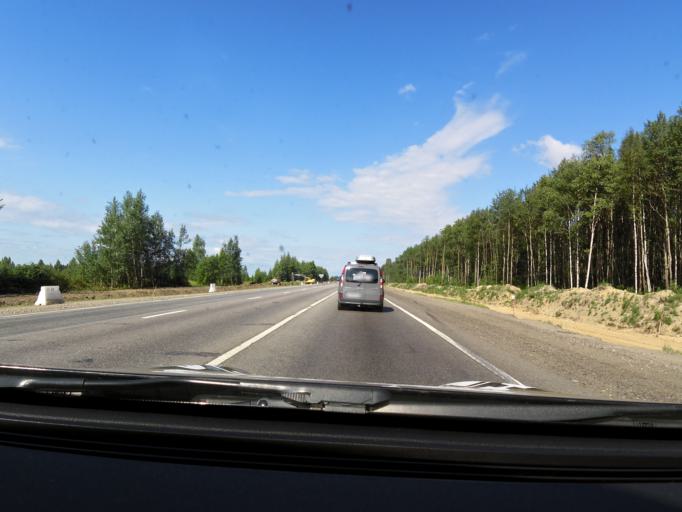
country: RU
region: Tverskaya
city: Emmaus
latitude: 56.7830
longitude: 36.0001
